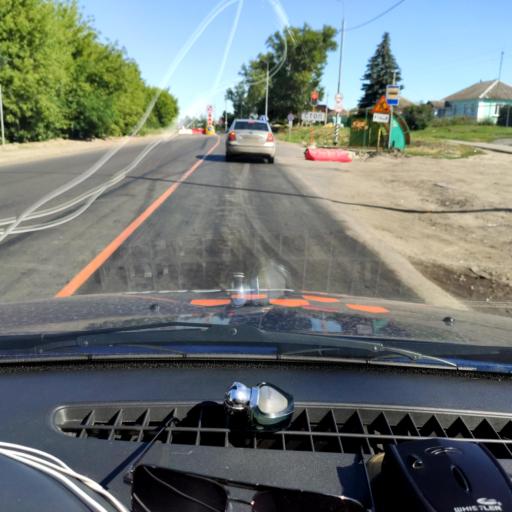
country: RU
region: Lipetsk
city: Khlevnoye
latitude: 52.1427
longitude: 39.1617
